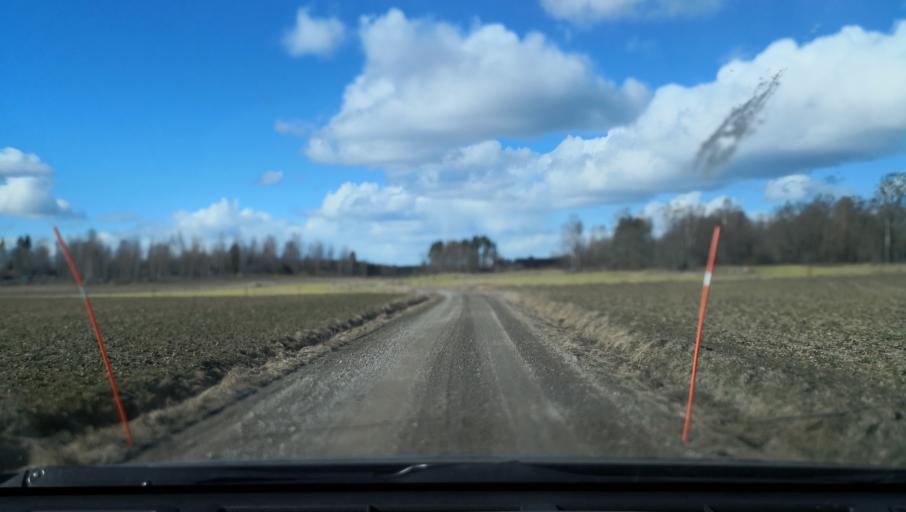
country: SE
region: OErebro
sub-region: Lindesbergs Kommun
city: Fellingsbro
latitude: 59.4217
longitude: 15.6292
